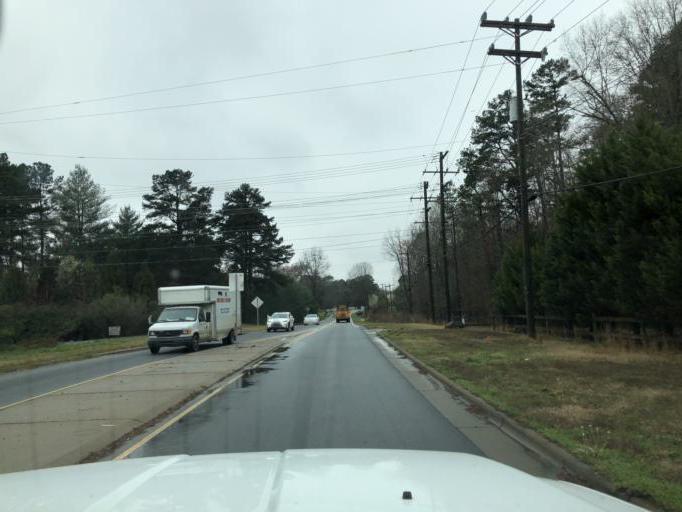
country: US
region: North Carolina
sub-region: Mecklenburg County
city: Huntersville
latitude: 35.3359
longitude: -80.9144
